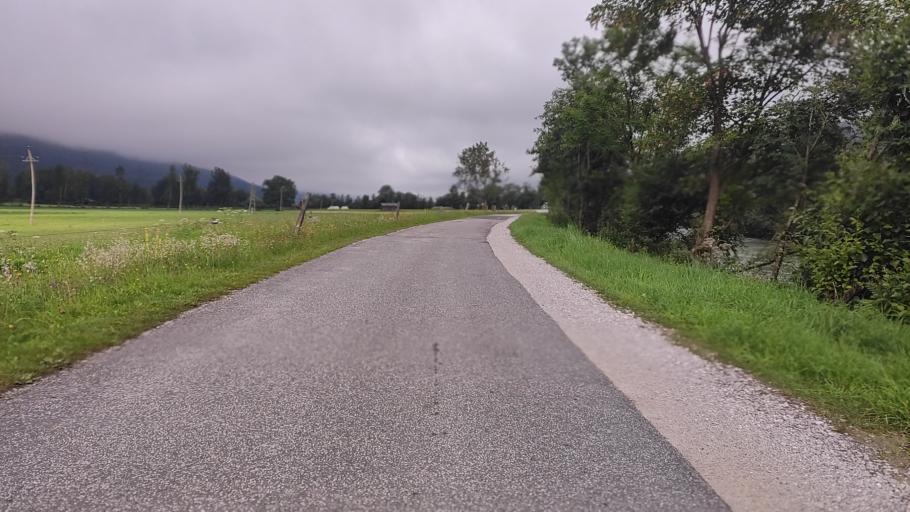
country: AT
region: Salzburg
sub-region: Politischer Bezirk Zell am See
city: Niedernsill
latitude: 47.2813
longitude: 12.6351
